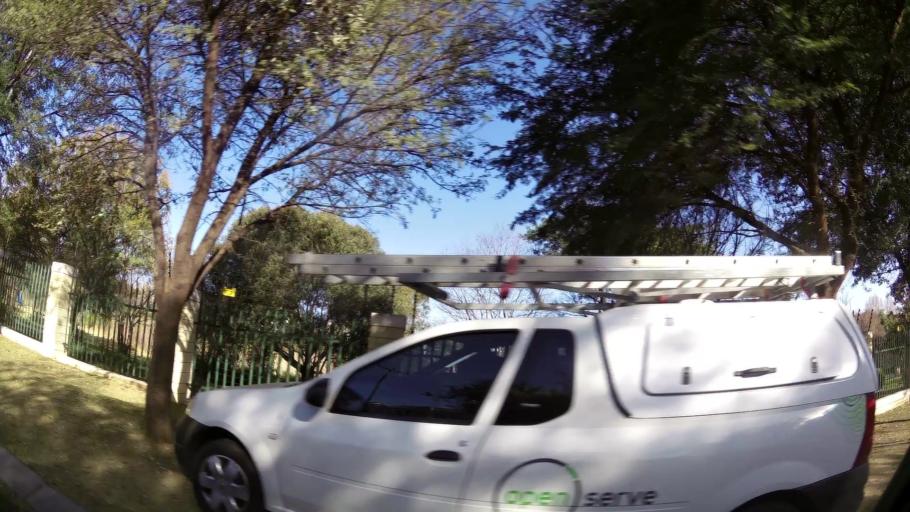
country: ZA
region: Gauteng
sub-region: City of Johannesburg Metropolitan Municipality
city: Diepsloot
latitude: -26.0205
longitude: 27.9969
